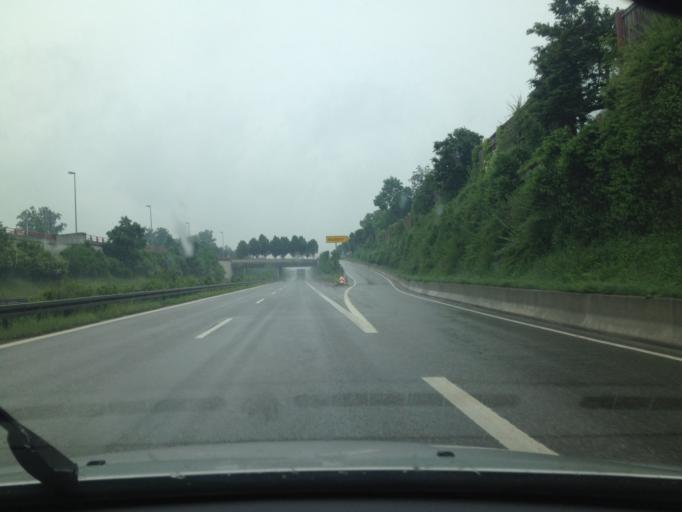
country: DE
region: Bavaria
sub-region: Swabia
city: Klosterlechfeld
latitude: 48.1722
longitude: 10.8394
